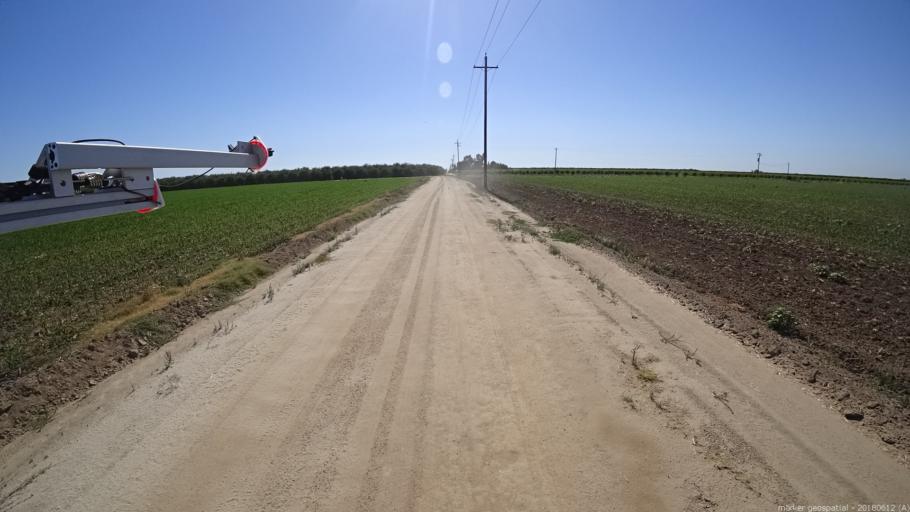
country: US
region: California
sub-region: Madera County
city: Chowchilla
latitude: 37.0108
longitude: -120.3662
